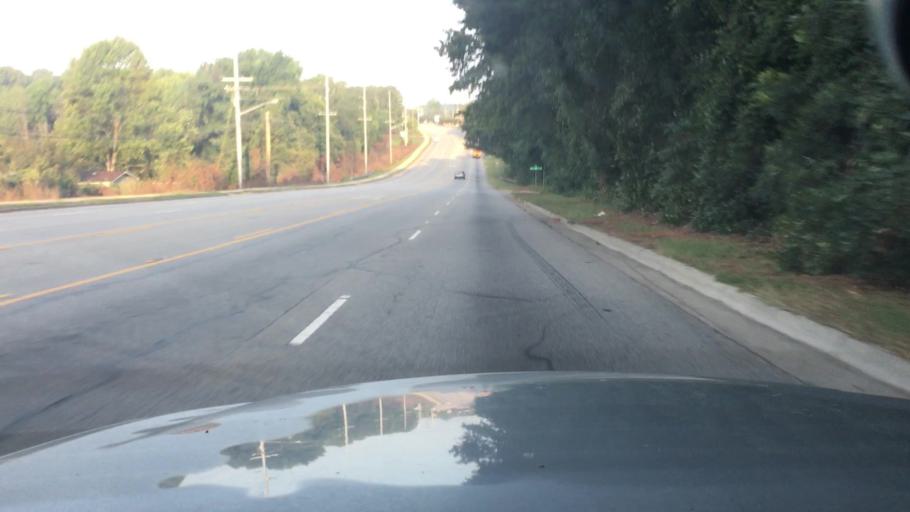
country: US
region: North Carolina
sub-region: Cumberland County
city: Fayetteville
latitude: 35.1042
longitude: -78.8913
